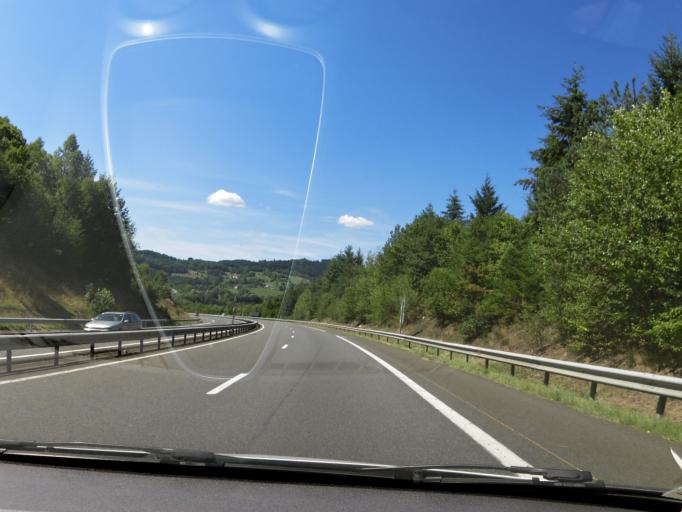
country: FR
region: Rhone-Alpes
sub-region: Departement de la Loire
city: Saint-Just-en-Chevalet
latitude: 45.8744
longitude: 3.8405
